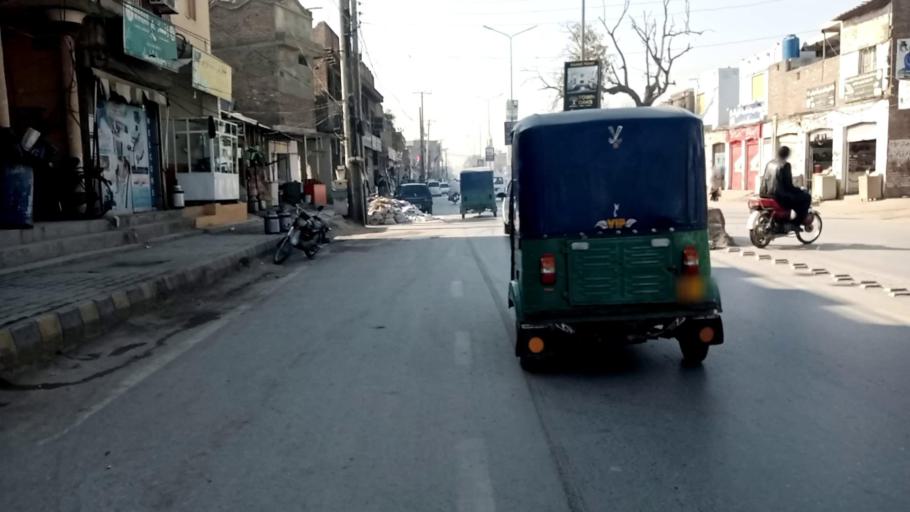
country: PK
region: Khyber Pakhtunkhwa
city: Peshawar
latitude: 33.9795
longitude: 71.5224
